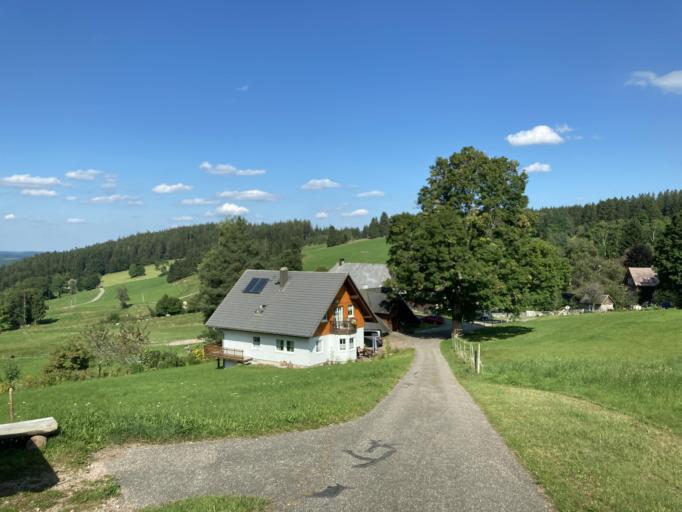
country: DE
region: Baden-Wuerttemberg
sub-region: Freiburg Region
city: Schonwald im Schwarzwald
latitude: 48.1061
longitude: 8.2294
